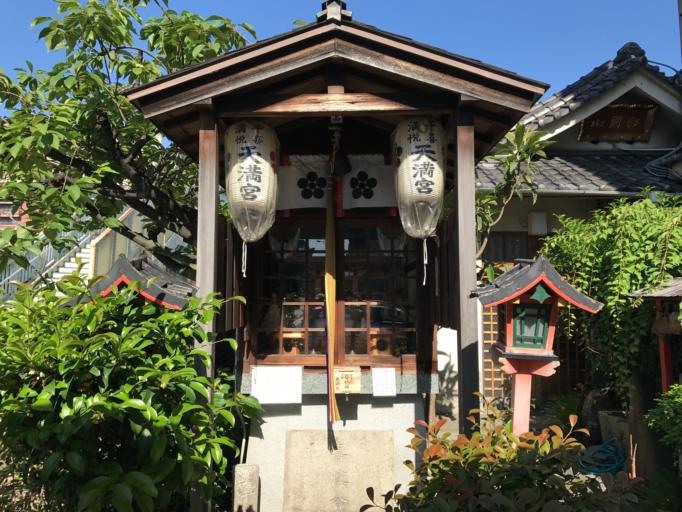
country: JP
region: Kyoto
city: Kyoto
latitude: 34.9960
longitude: 135.7628
